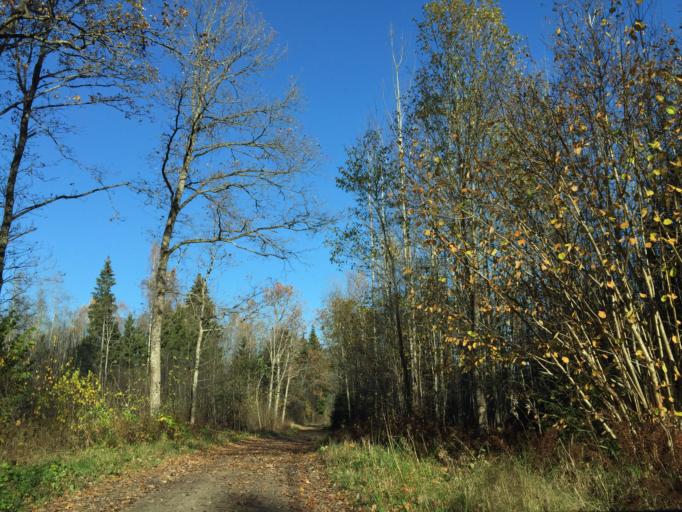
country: LV
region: Aizkraukles Rajons
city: Aizkraukle
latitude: 56.5735
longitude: 25.1778
